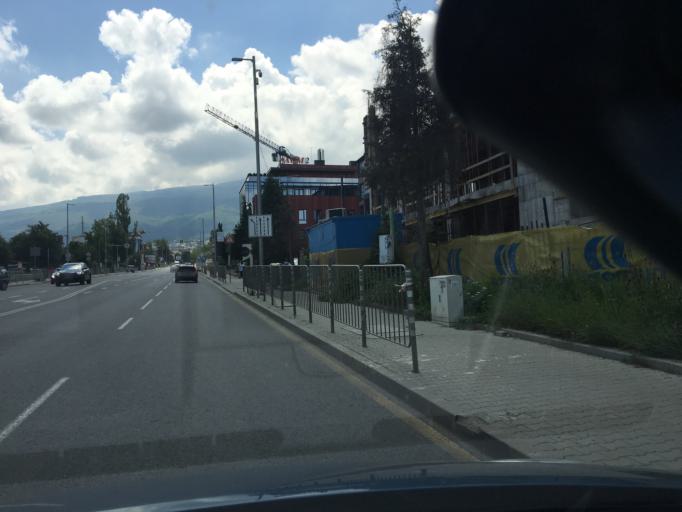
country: BG
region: Sofia-Capital
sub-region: Stolichna Obshtina
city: Sofia
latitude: 42.6493
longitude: 23.3153
